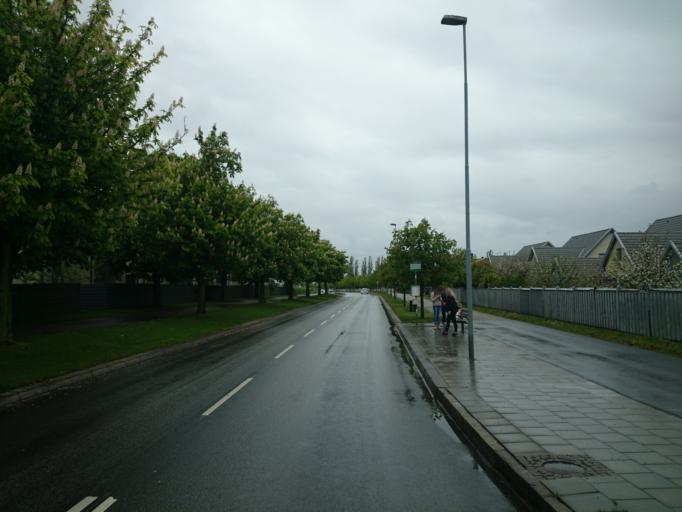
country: SE
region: Skane
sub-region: Malmo
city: Bunkeflostrand
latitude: 55.5544
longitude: 12.9277
